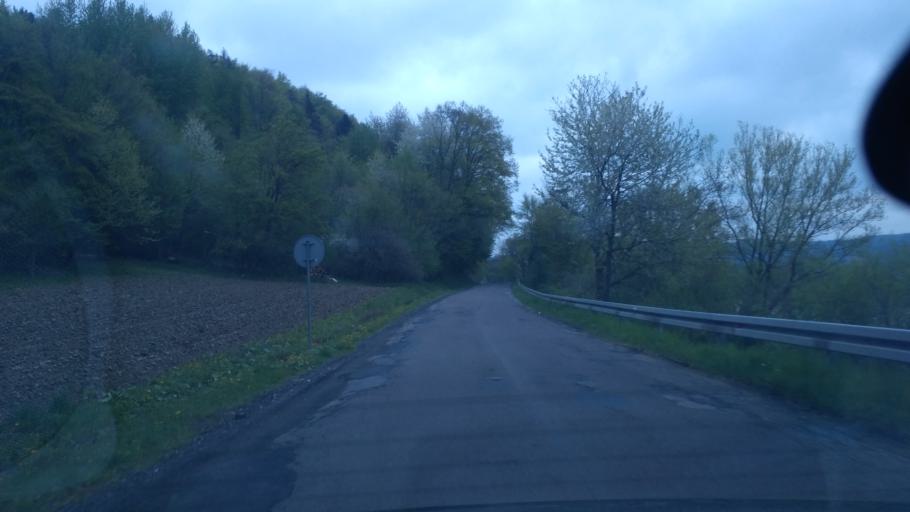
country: PL
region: Subcarpathian Voivodeship
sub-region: Powiat brzozowski
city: Nozdrzec
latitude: 49.7404
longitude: 22.2068
